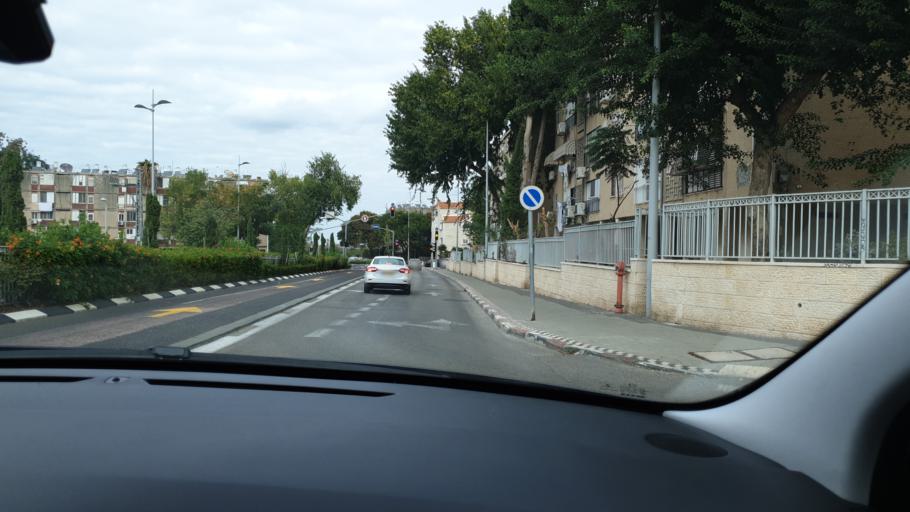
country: IL
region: Haifa
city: Qiryat Ata
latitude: 32.8157
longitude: 35.1135
